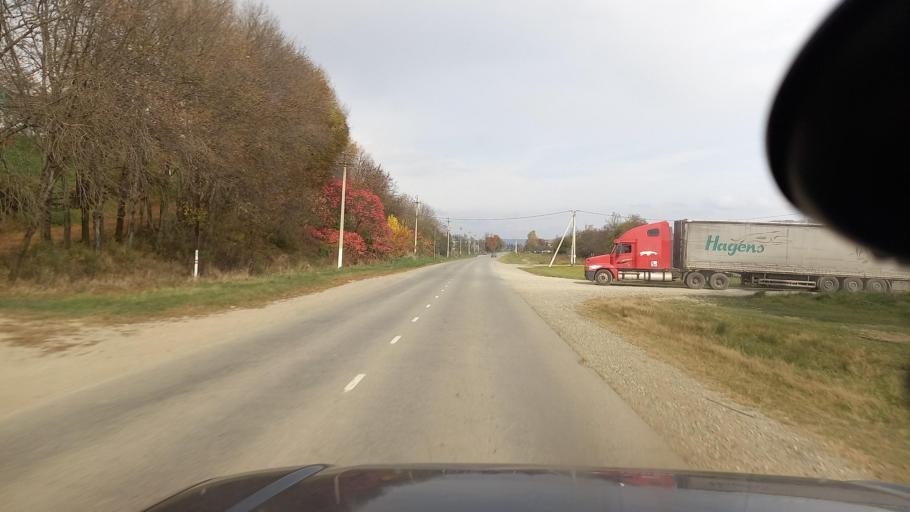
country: RU
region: Krasnodarskiy
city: Psebay
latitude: 44.1345
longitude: 40.8147
